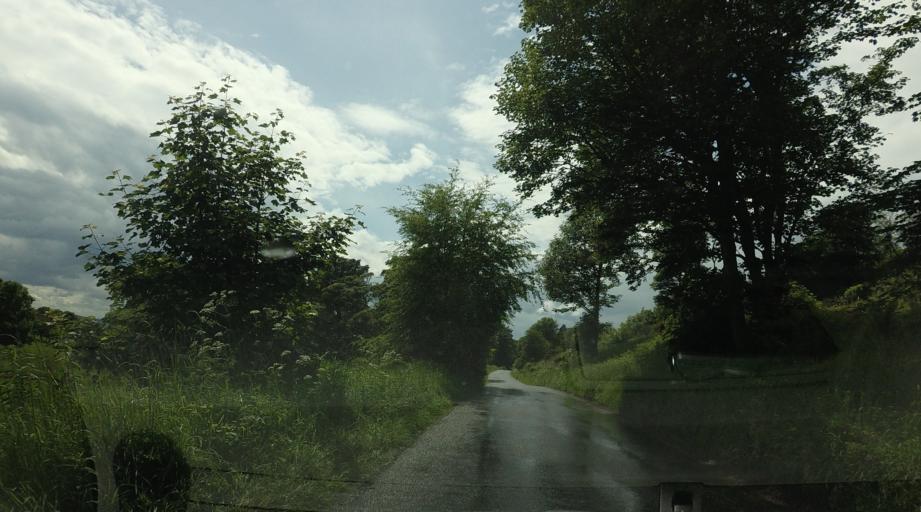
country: GB
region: Scotland
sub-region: Fife
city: Ballingry
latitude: 56.1577
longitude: -3.3568
